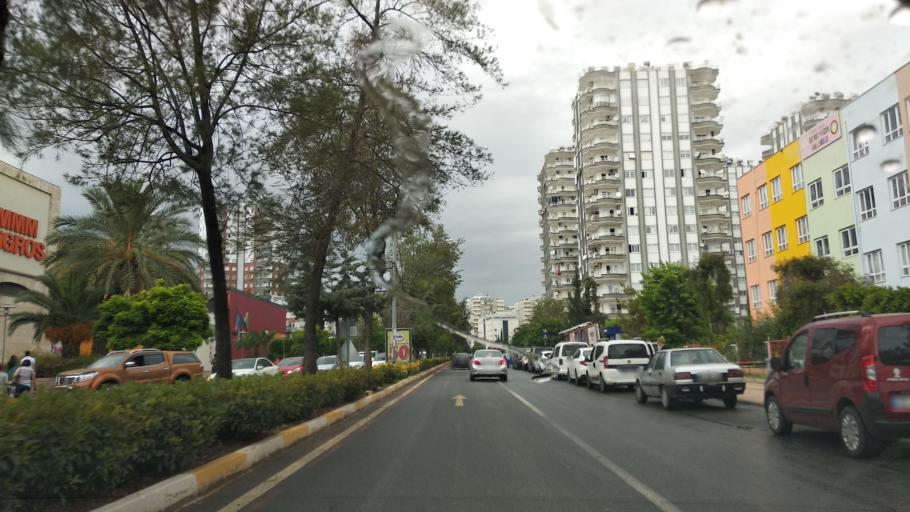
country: TR
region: Mersin
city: Mercin
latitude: 36.7856
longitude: 34.5891
